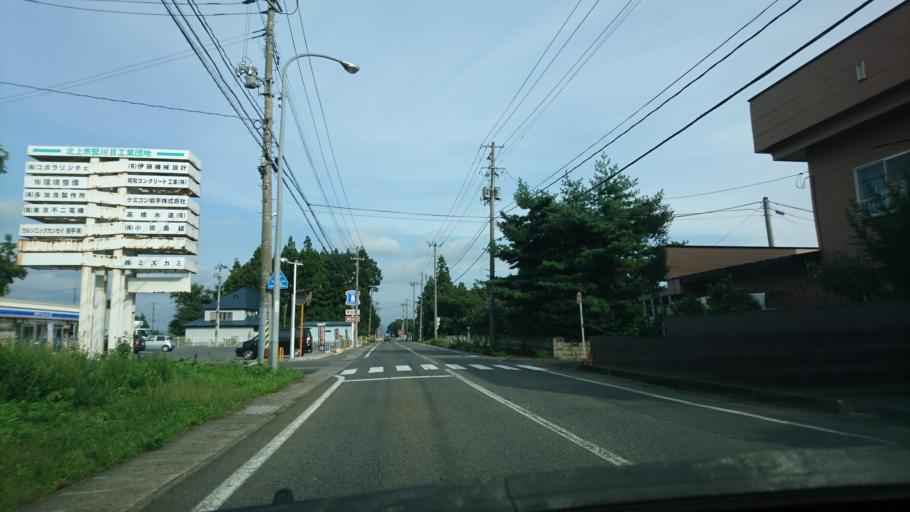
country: JP
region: Iwate
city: Kitakami
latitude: 39.3067
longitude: 141.0013
